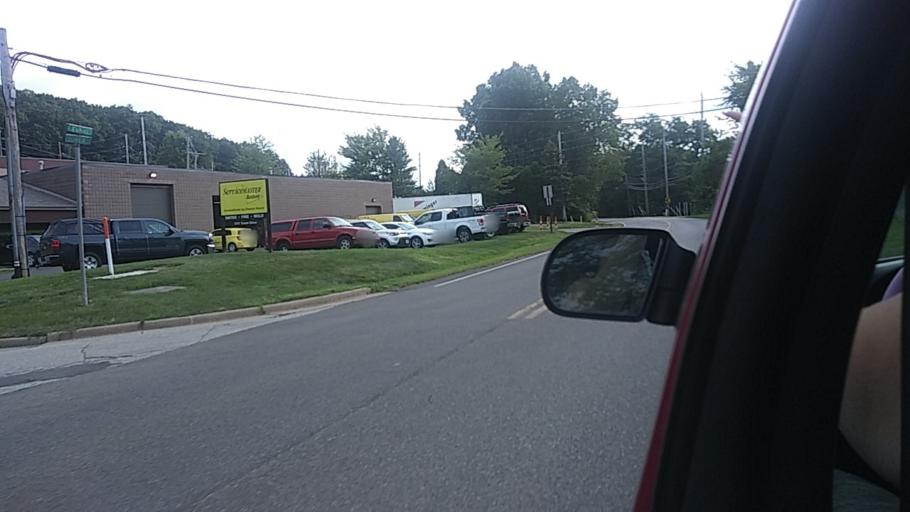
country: US
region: Ohio
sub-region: Summit County
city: Tallmadge
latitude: 41.0930
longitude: -81.4757
